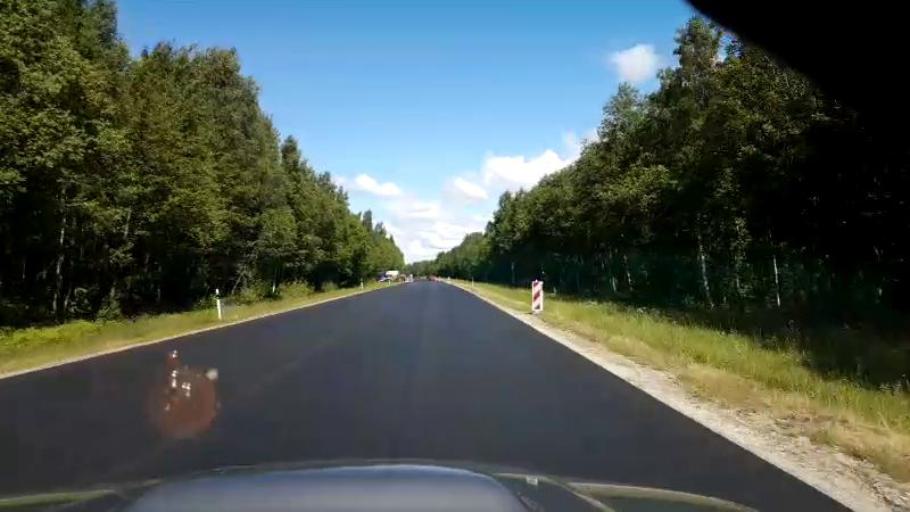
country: LV
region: Salacgrivas
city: Ainazi
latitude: 58.0192
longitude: 24.4980
